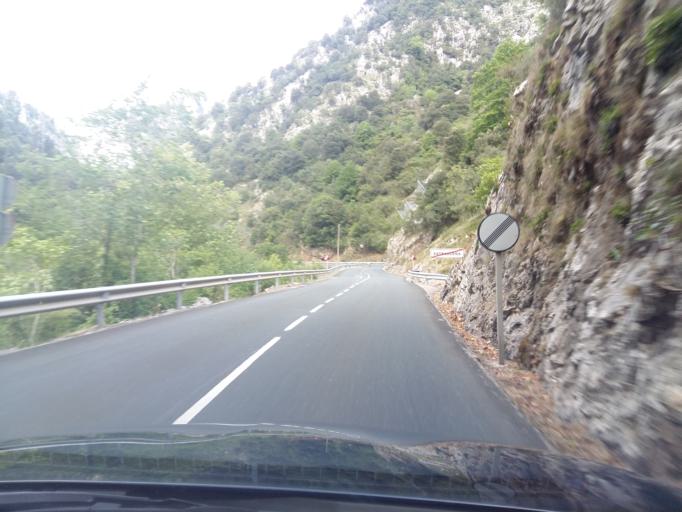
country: ES
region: Cantabria
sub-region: Provincia de Cantabria
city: Tresviso
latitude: 43.2912
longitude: -4.6166
